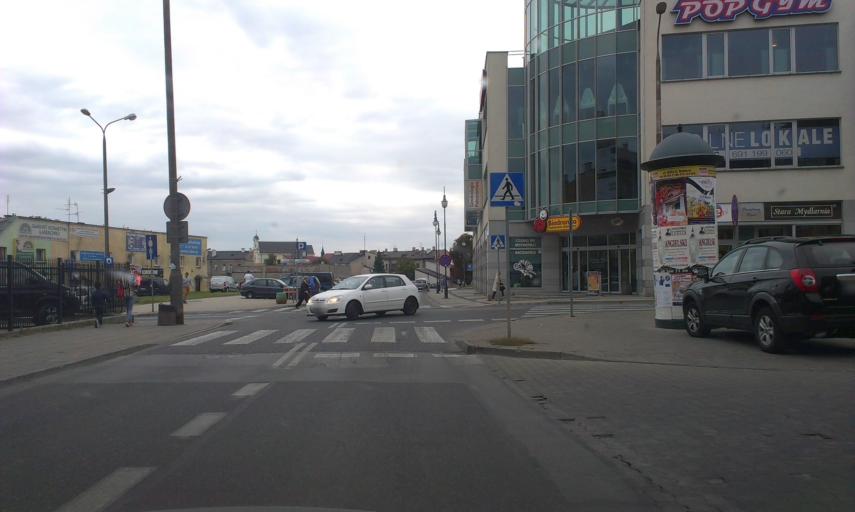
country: PL
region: Masovian Voivodeship
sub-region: Radom
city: Radom
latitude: 51.4026
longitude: 21.1522
